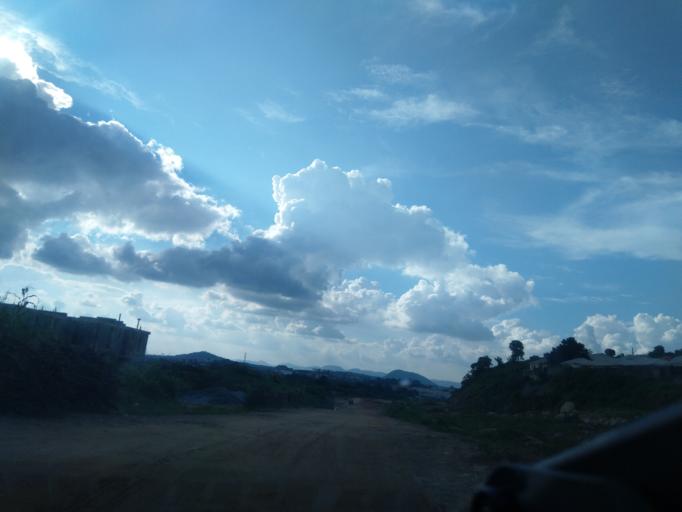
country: NG
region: Abuja Federal Capital Territory
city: Abuja
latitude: 9.0517
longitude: 7.4005
